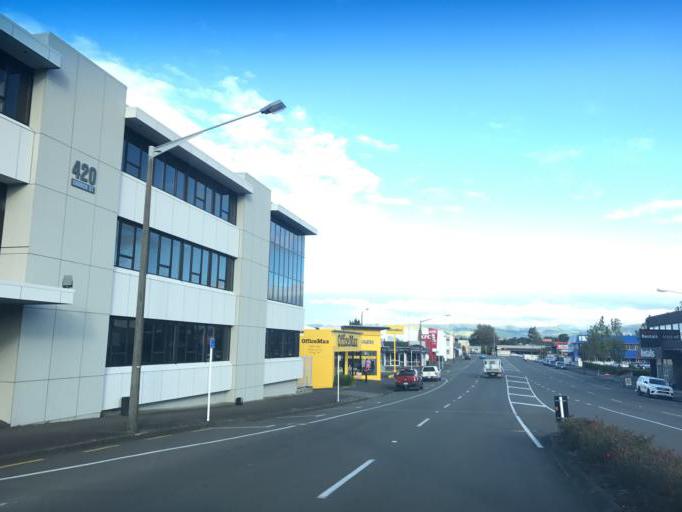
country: NZ
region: Manawatu-Wanganui
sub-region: Palmerston North City
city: Palmerston North
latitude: -40.3554
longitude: 175.6164
